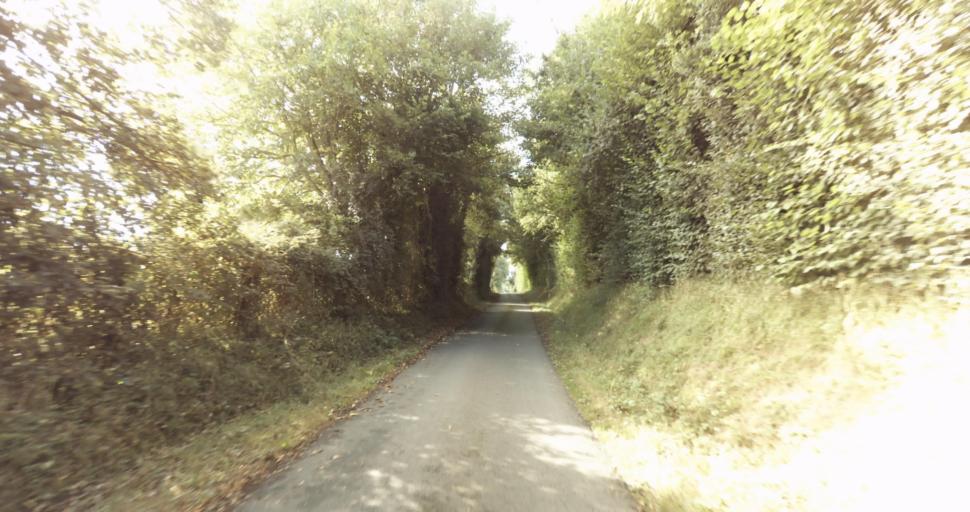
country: FR
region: Lower Normandy
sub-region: Departement de l'Orne
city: Vimoutiers
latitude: 48.9149
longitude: 0.1246
